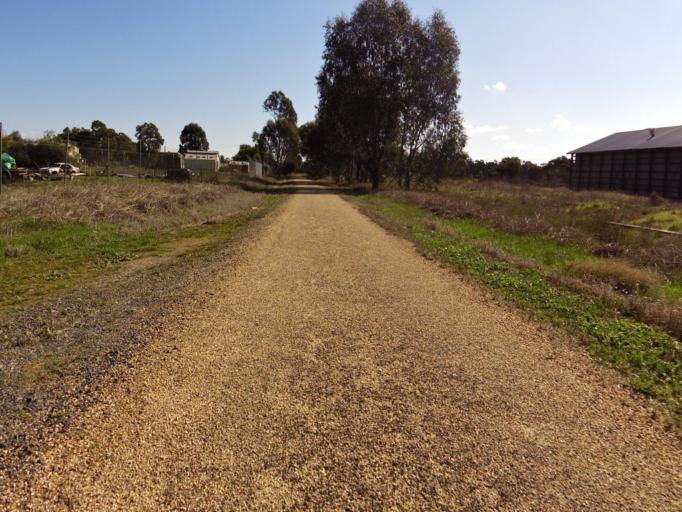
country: AU
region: New South Wales
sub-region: Corowa Shire
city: Corowa
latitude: -36.0119
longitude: 146.4054
